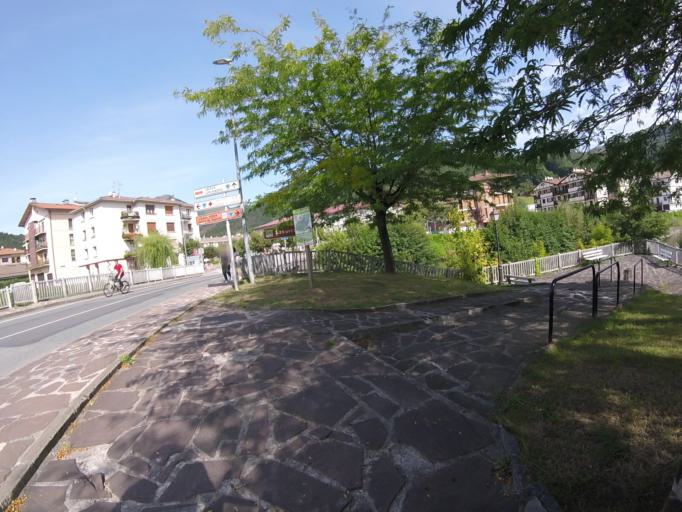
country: ES
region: Navarre
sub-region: Provincia de Navarra
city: Doneztebe
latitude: 43.1316
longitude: -1.6720
